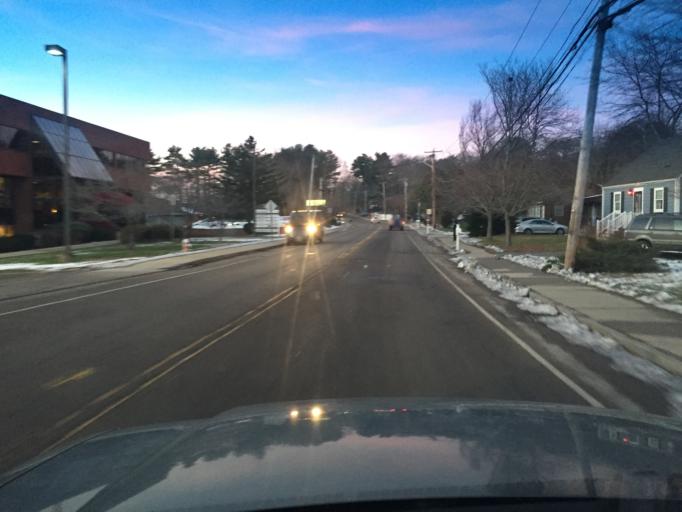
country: US
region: Massachusetts
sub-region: Norfolk County
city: Franklin
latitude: 42.0913
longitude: -71.4256
